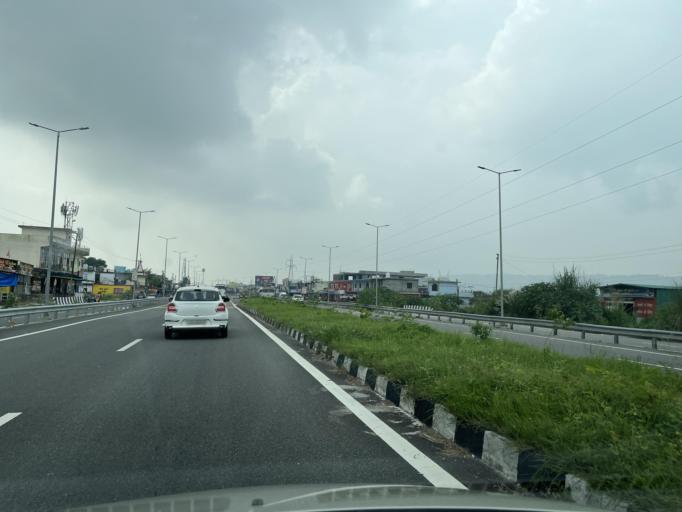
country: IN
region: Uttarakhand
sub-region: Dehradun
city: Raiwala
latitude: 30.0825
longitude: 78.1904
